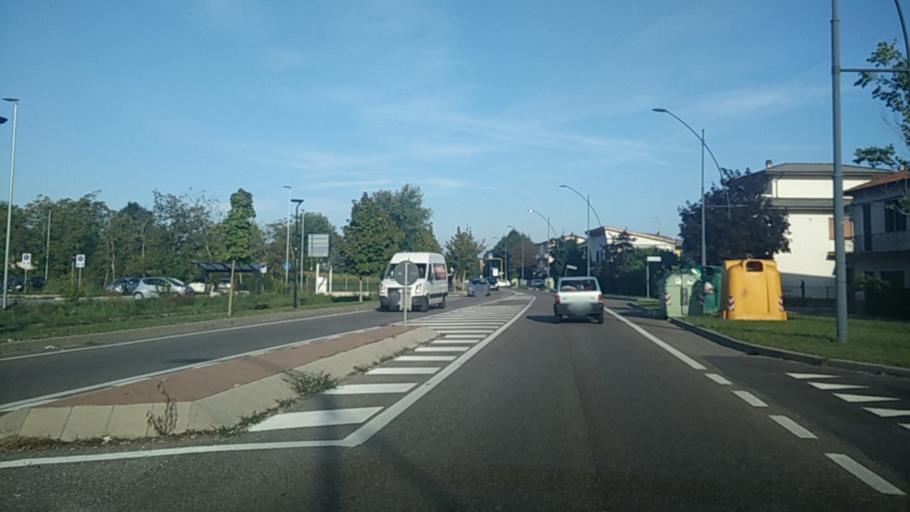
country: IT
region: Veneto
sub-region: Provincia di Venezia
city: Trivignano
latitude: 45.5245
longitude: 12.1945
